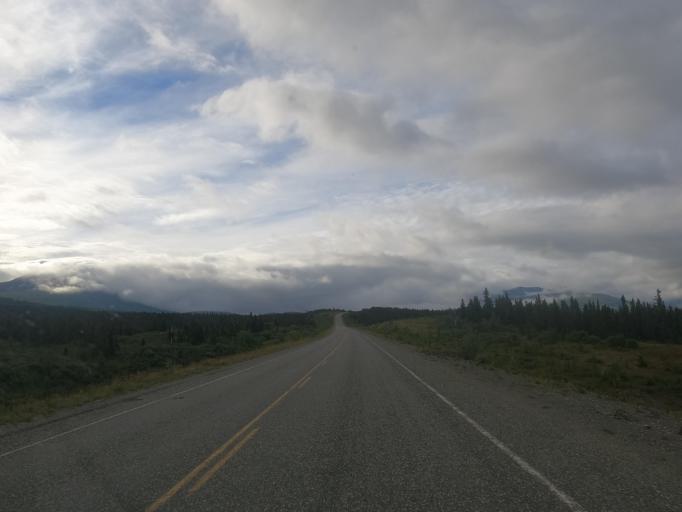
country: CA
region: Yukon
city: Haines Junction
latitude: 59.9531
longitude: -136.8079
